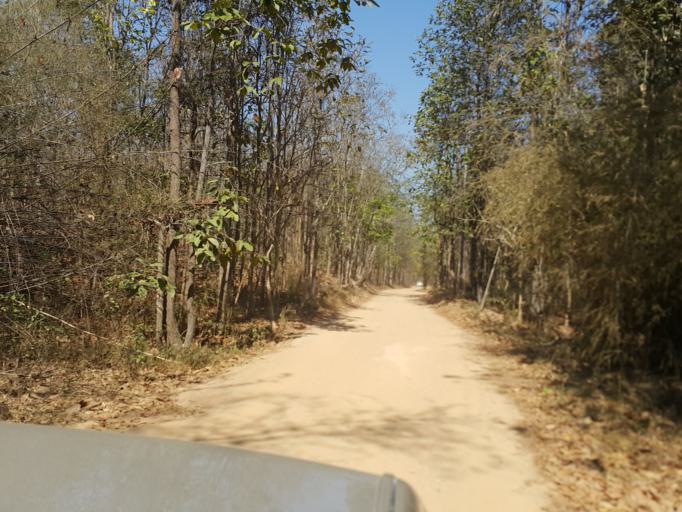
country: TH
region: Chiang Mai
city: Doi Lo
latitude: 18.5257
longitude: 98.7446
